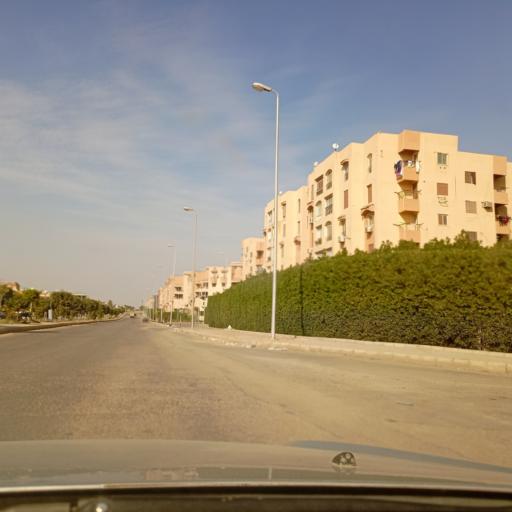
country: EG
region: Muhafazat al Qalyubiyah
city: Al Khankah
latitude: 30.0415
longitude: 31.4852
